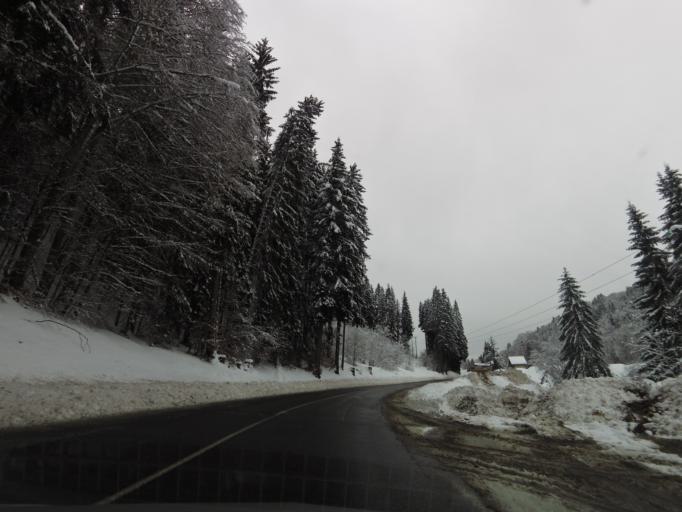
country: FR
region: Rhone-Alpes
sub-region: Departement de la Haute-Savoie
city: Morzine
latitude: 46.1783
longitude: 6.6832
